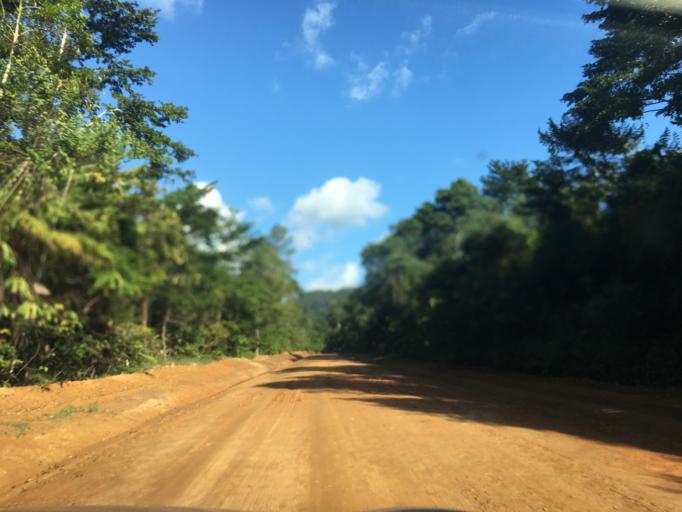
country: BZ
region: Stann Creek
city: Placencia
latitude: 16.7841
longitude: -88.4552
